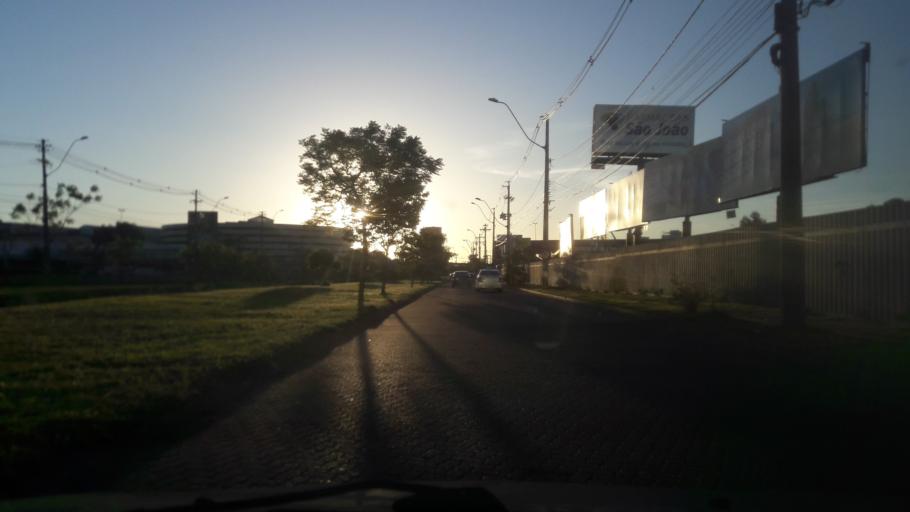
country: BR
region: Rio Grande do Sul
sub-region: Canoas
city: Canoas
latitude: -29.9878
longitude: -51.1730
